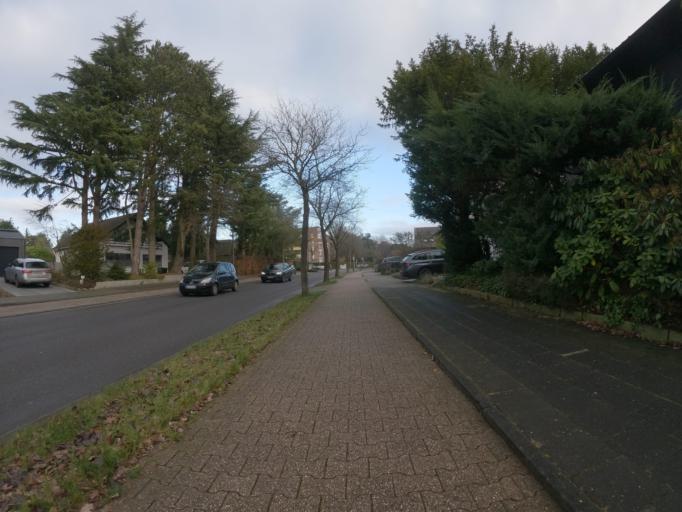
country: DE
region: North Rhine-Westphalia
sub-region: Regierungsbezirk Koln
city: Aachen
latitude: 50.8076
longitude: 6.0700
